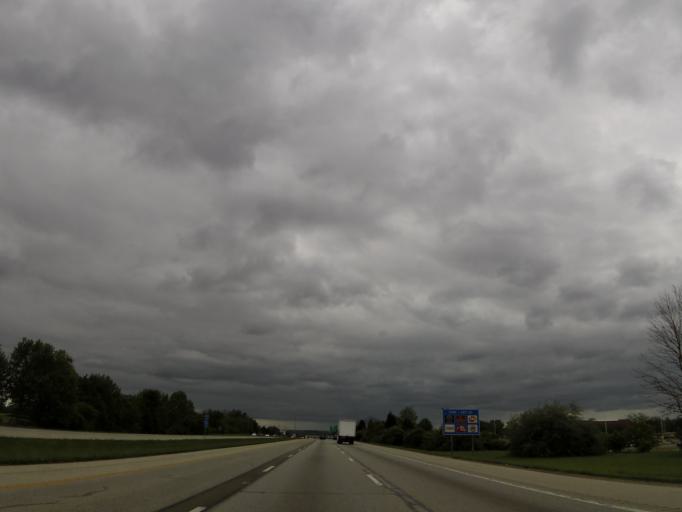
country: US
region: Ohio
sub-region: Warren County
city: Kings Mills
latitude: 39.3471
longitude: -84.2736
